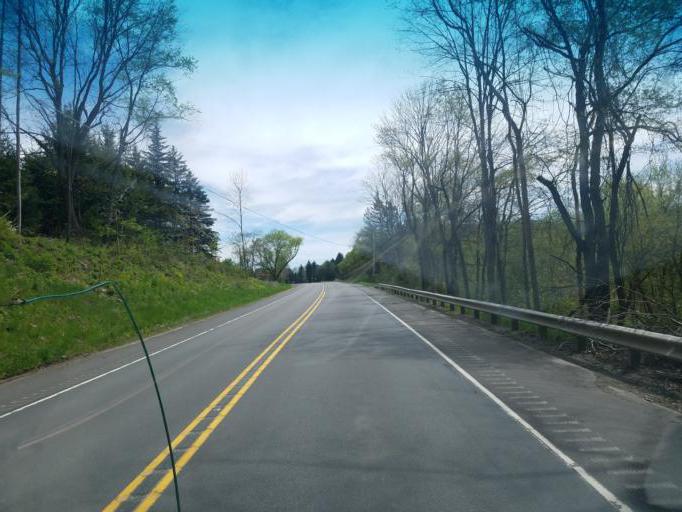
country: US
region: Pennsylvania
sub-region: Potter County
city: Galeton
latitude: 41.7457
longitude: -77.5961
